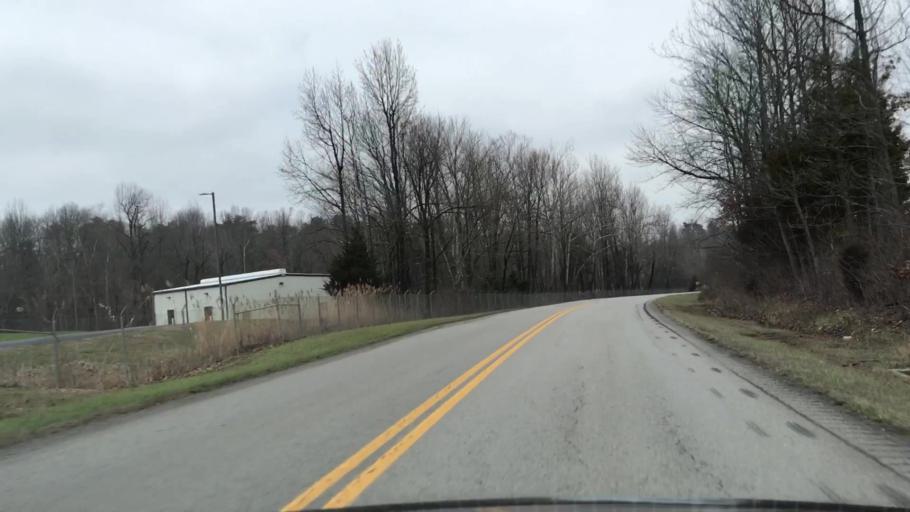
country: US
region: Kentucky
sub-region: Muhlenberg County
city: Morehead
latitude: 37.2608
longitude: -87.2091
